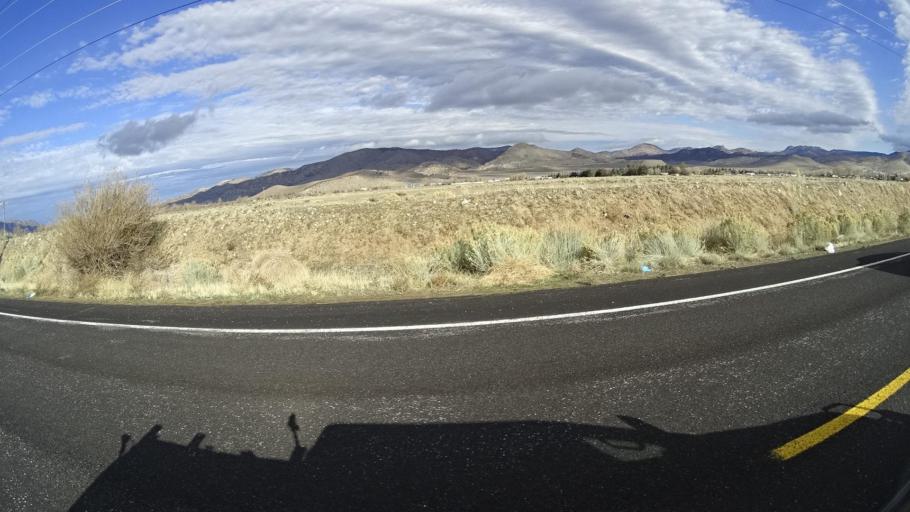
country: US
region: California
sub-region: Kern County
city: Tehachapi
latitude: 35.1097
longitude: -118.4044
